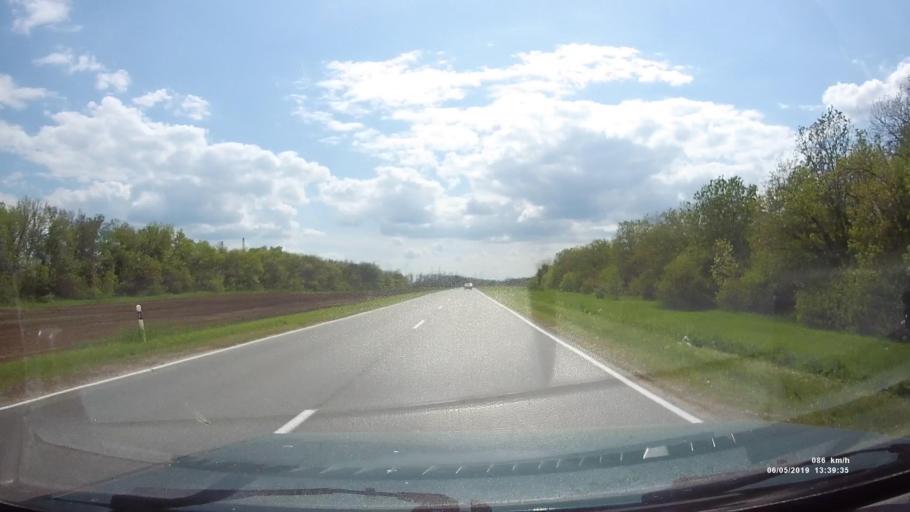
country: RU
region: Rostov
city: Ust'-Donetskiy
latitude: 47.6741
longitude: 40.7016
